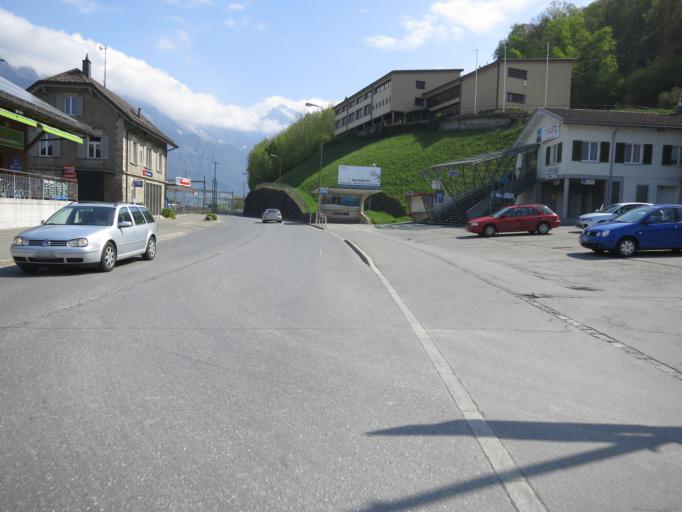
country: CH
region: Saint Gallen
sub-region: Wahlkreis Sarganserland
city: Quarten
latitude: 47.1136
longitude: 9.2545
